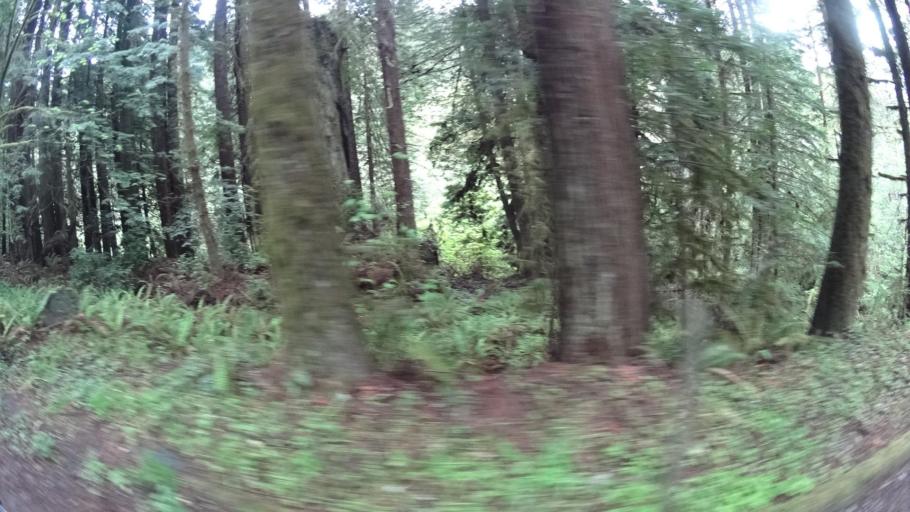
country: US
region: California
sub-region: Humboldt County
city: Bayside
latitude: 40.8195
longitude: -124.0302
